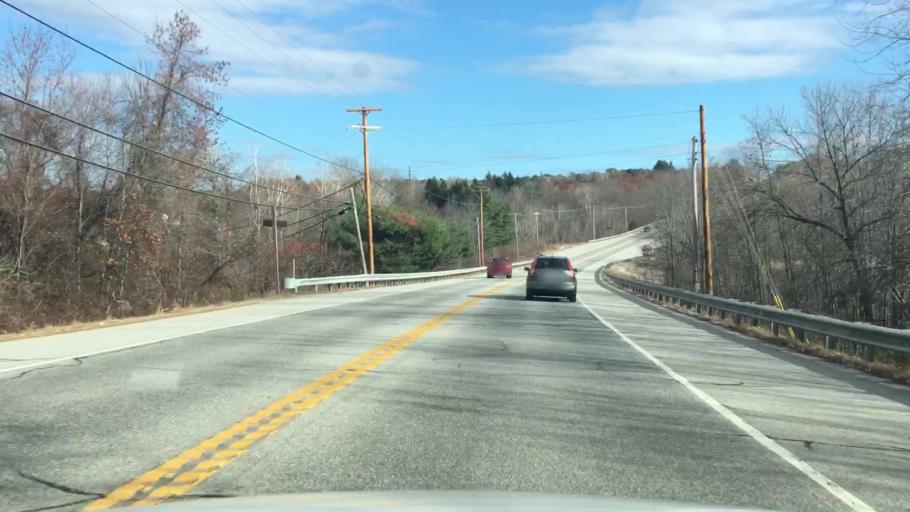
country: US
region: Maine
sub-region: Kennebec County
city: Winthrop
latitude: 44.3017
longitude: -69.9752
